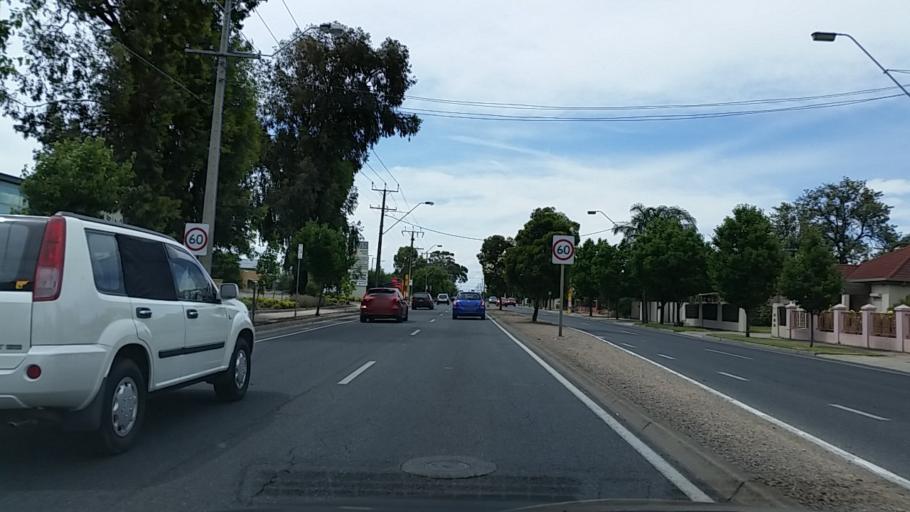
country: AU
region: South Australia
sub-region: City of West Torrens
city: Plympton
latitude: -34.9478
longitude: 138.5536
